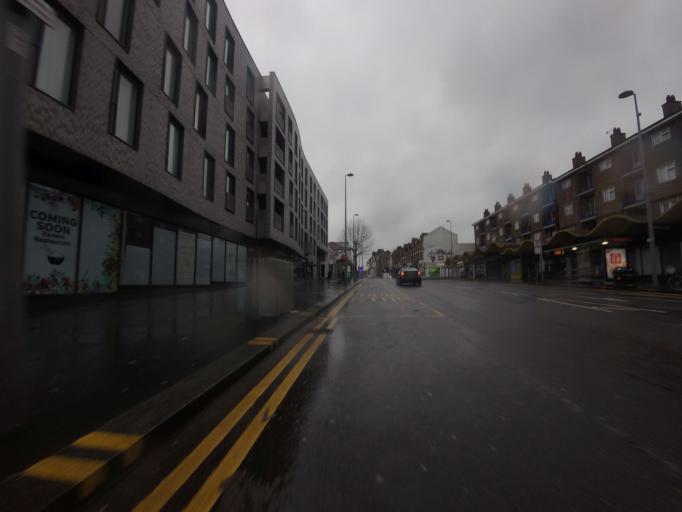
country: GB
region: England
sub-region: Greater London
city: Walthamstow
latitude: 51.5852
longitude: -0.0196
